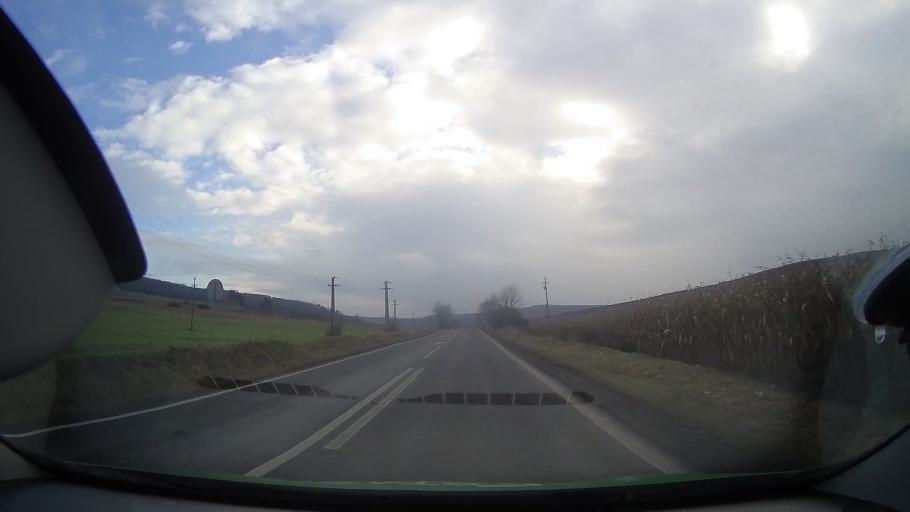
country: RO
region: Mures
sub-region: Comuna Cucerdea
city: Cucerdea
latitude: 46.3787
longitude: 24.2560
